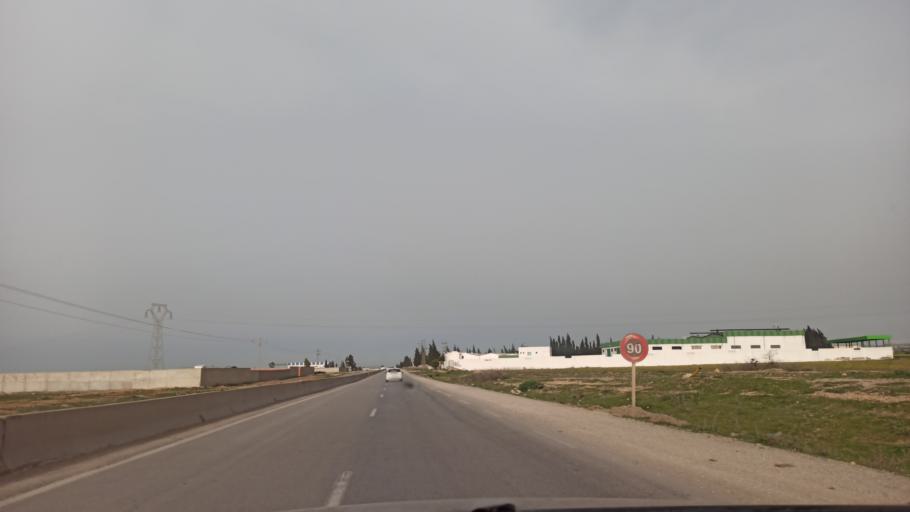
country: TN
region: Tunis
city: La Mohammedia
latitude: 36.5703
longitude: 10.0861
